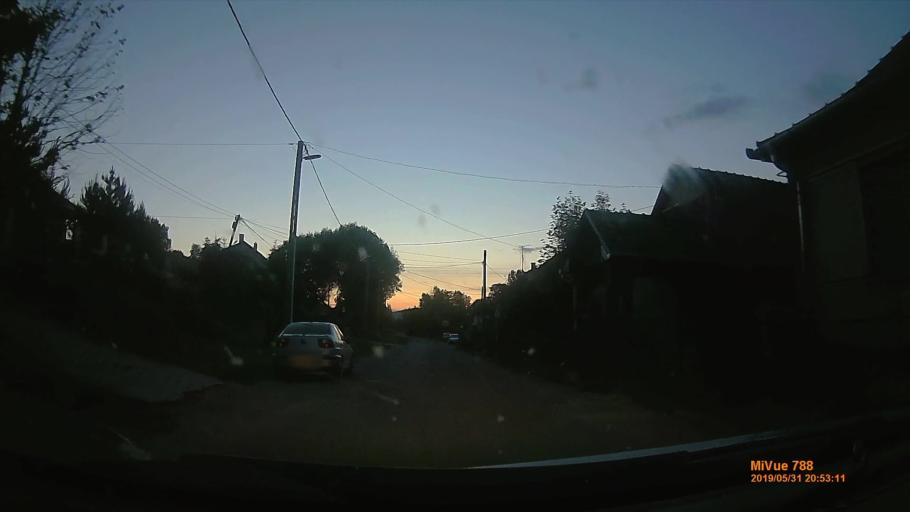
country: HU
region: Nograd
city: Nagyoroszi
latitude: 48.0482
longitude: 19.0515
